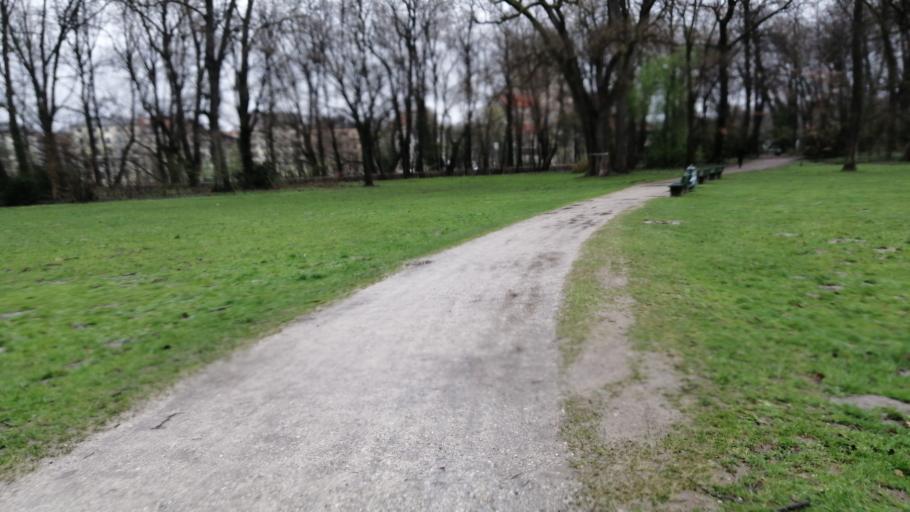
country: DE
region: Bavaria
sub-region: Upper Bavaria
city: Munich
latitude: 48.1241
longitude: 11.5748
